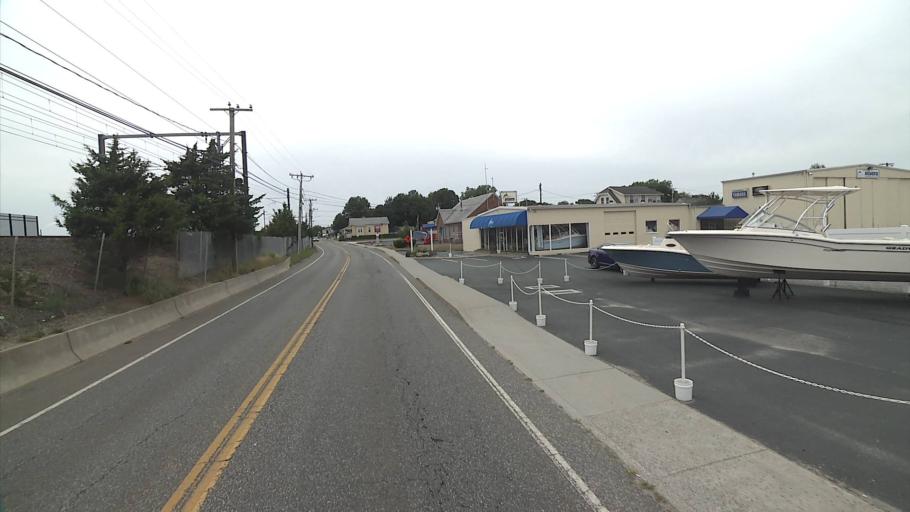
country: US
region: Connecticut
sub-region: New London County
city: Niantic
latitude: 41.3246
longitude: -72.1859
